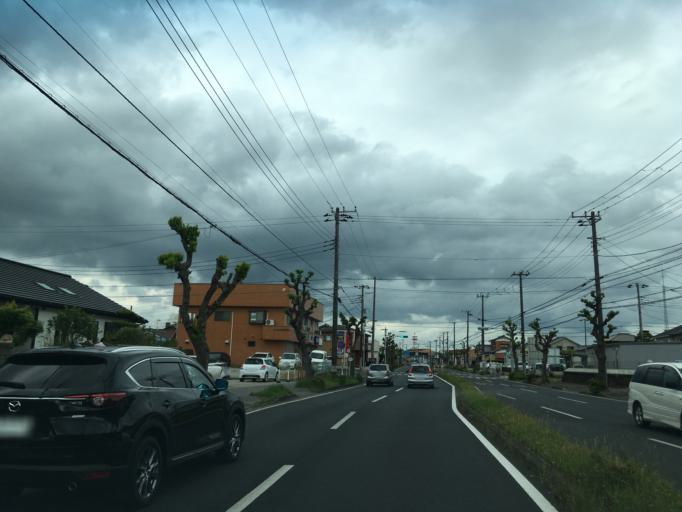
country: JP
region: Chiba
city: Kimitsu
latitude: 35.3304
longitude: 139.8940
